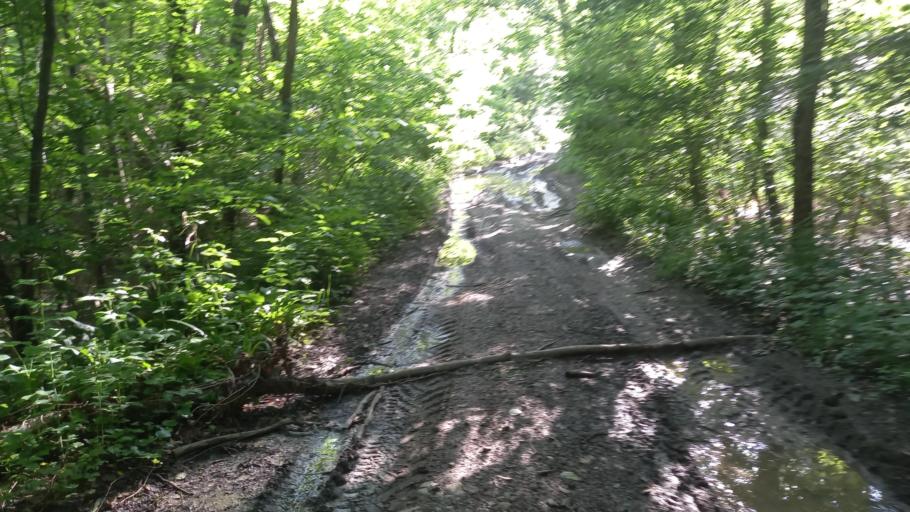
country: RU
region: Krasnodarskiy
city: Dzhubga
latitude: 44.5351
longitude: 38.7367
